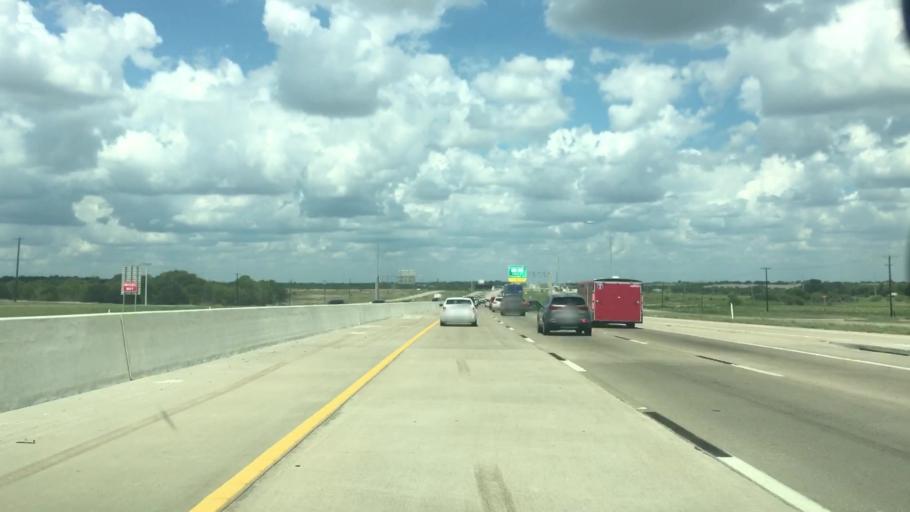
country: US
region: Texas
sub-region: McLennan County
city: Lorena
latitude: 31.4012
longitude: -97.2059
